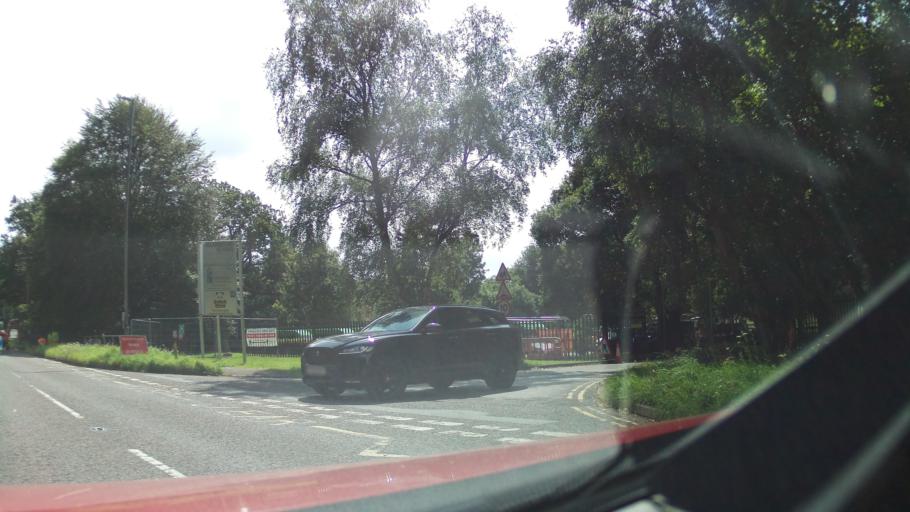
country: GB
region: England
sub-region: Dorset
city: Blandford Forum
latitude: 50.8649
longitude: -2.1701
